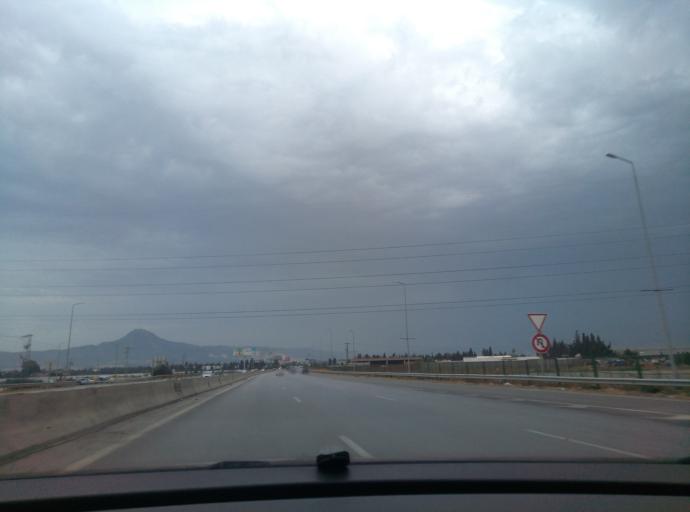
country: TN
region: Bin 'Arus
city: Ben Arous
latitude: 36.7249
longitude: 10.2559
